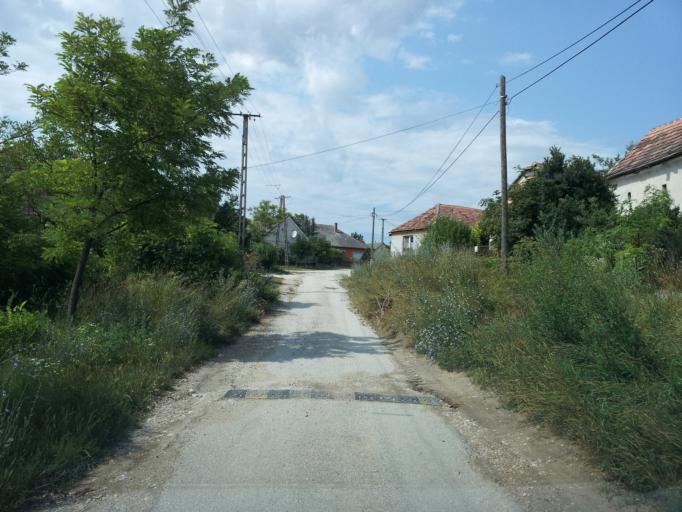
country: HU
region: Fejer
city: Enying
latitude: 46.9376
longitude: 18.2381
